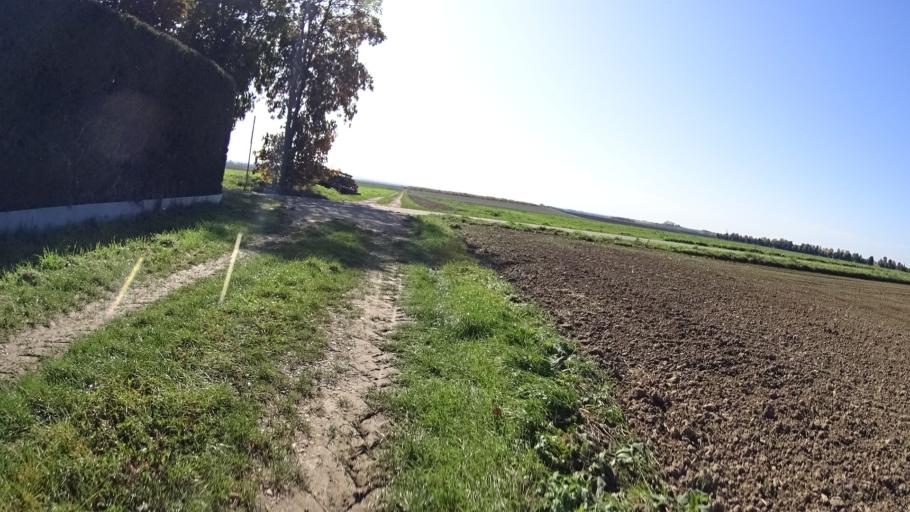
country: DE
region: Bavaria
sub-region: Upper Bavaria
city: Gaimersheim
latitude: 48.8339
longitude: 11.3510
